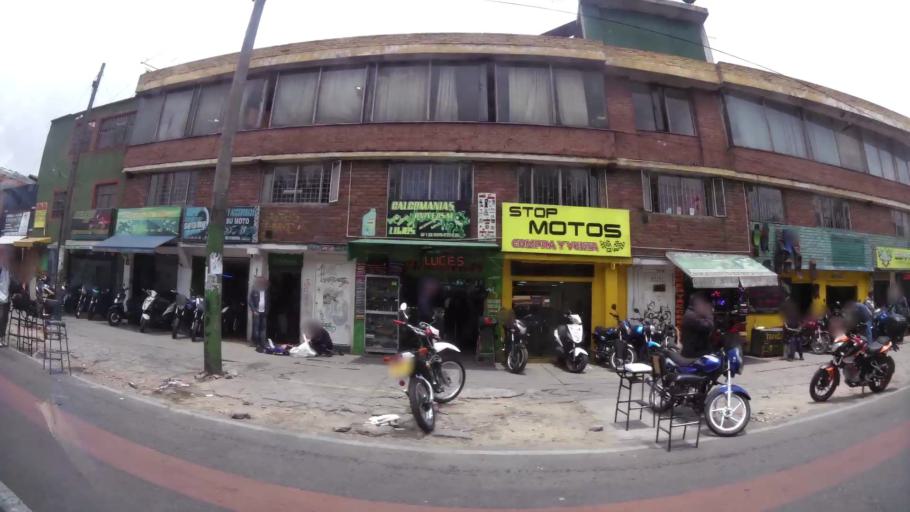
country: CO
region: Bogota D.C.
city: Bogota
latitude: 4.5919
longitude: -74.1107
